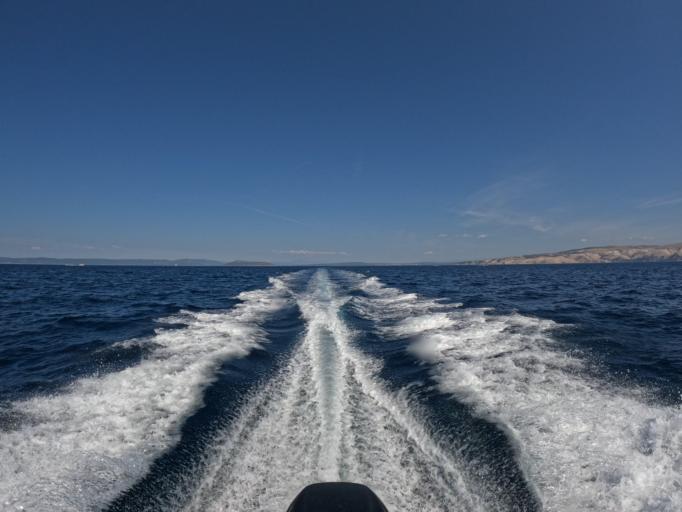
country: HR
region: Primorsko-Goranska
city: Lopar
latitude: 44.8975
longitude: 14.6386
